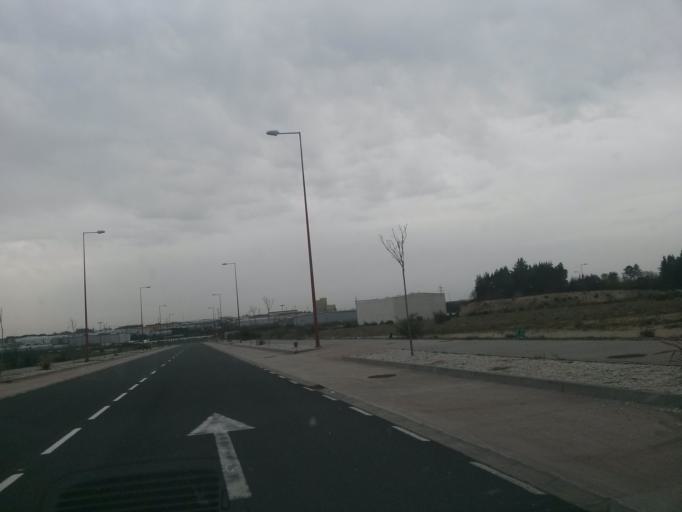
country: ES
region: Galicia
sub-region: Provincia de Lugo
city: Lugo
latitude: 43.0443
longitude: -7.5494
